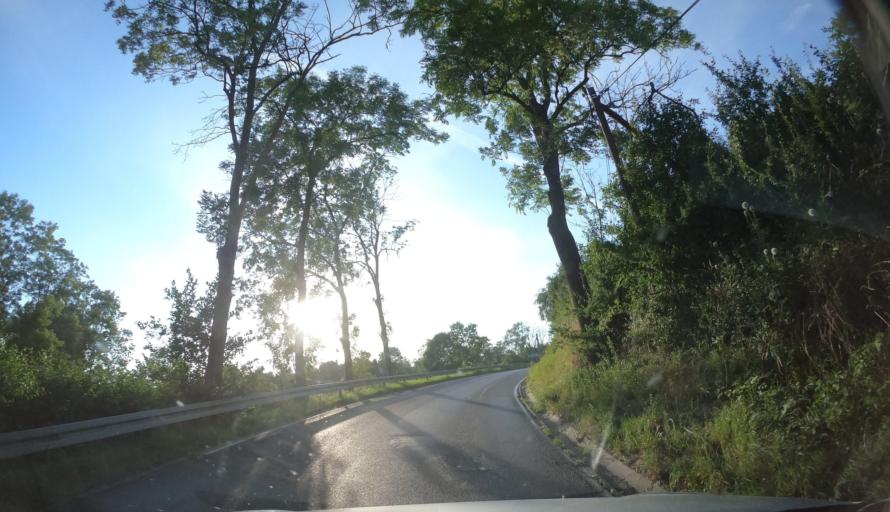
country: PL
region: Kujawsko-Pomorskie
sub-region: Bydgoszcz
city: Fordon
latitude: 53.2089
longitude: 18.1701
